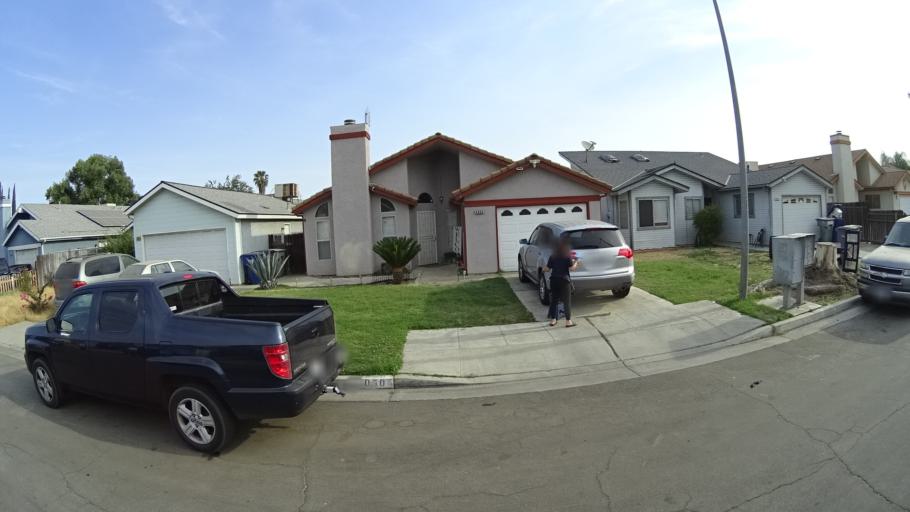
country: US
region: California
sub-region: Fresno County
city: West Park
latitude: 36.7744
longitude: -119.8636
